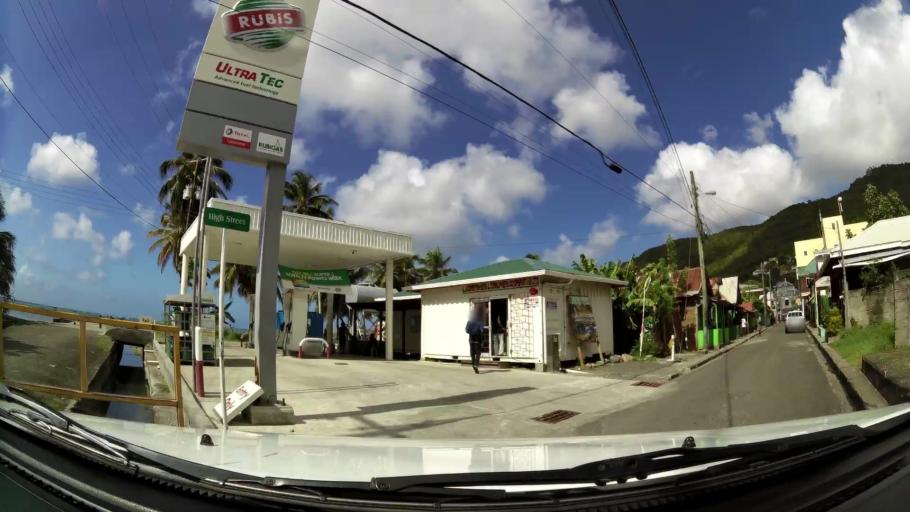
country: LC
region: Laborie Quarter
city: Laborie
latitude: 13.7502
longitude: -60.9952
